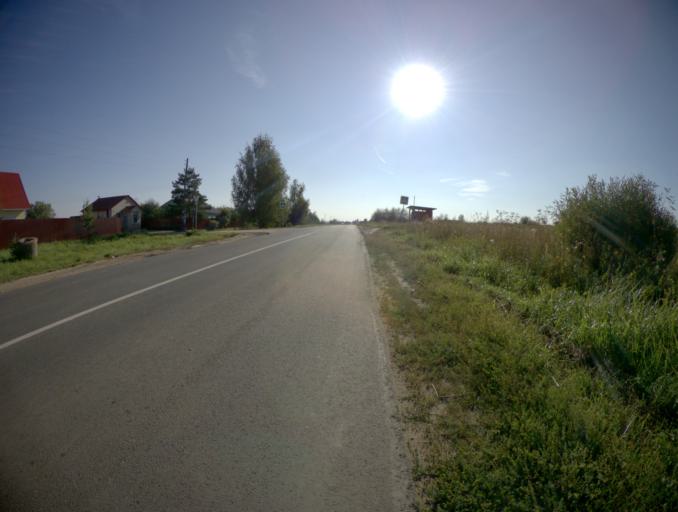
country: RU
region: Vladimir
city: Orgtrud
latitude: 56.3070
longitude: 40.5942
